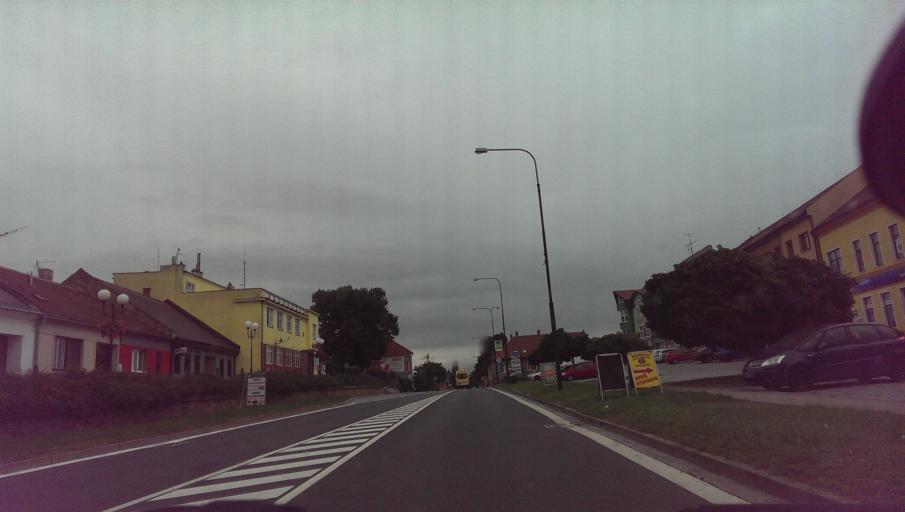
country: CZ
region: South Moravian
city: Bzenec
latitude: 48.9726
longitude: 17.2678
